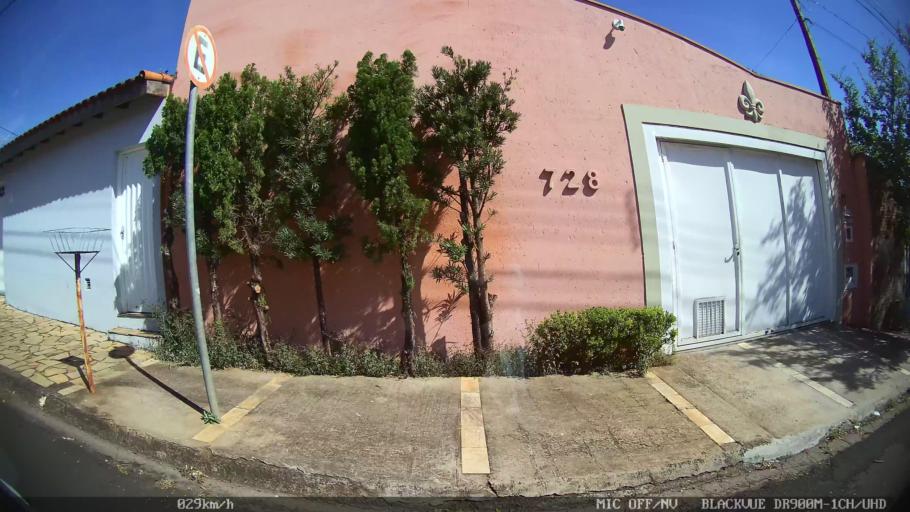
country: BR
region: Sao Paulo
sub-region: Franca
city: Franca
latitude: -20.5569
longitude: -47.3998
